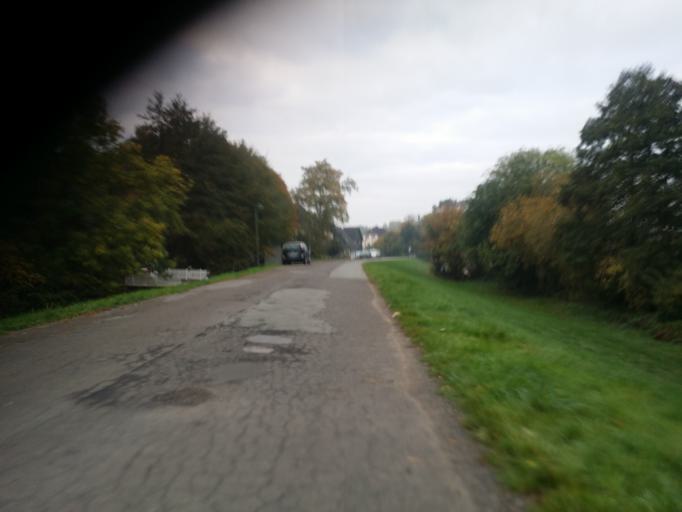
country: DE
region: Lower Saxony
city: Ritterhude
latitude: 53.1576
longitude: 8.7089
